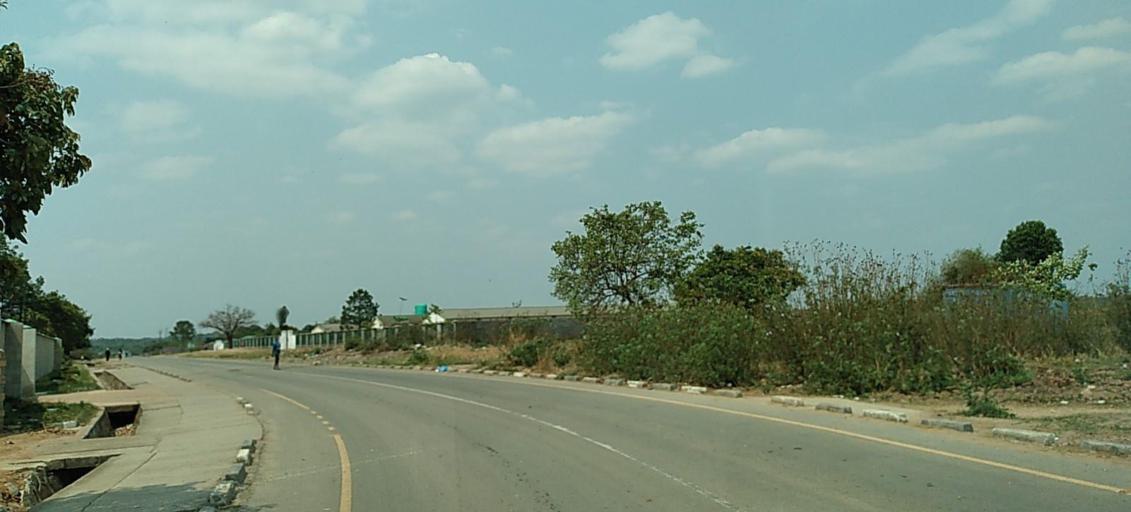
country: ZM
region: Copperbelt
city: Chambishi
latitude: -12.6317
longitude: 28.0591
